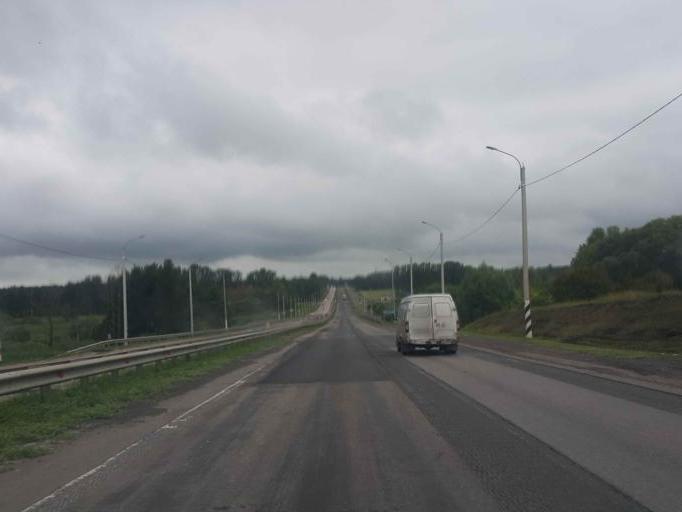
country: RU
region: Tambov
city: Selezni
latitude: 52.7449
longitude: 41.1977
